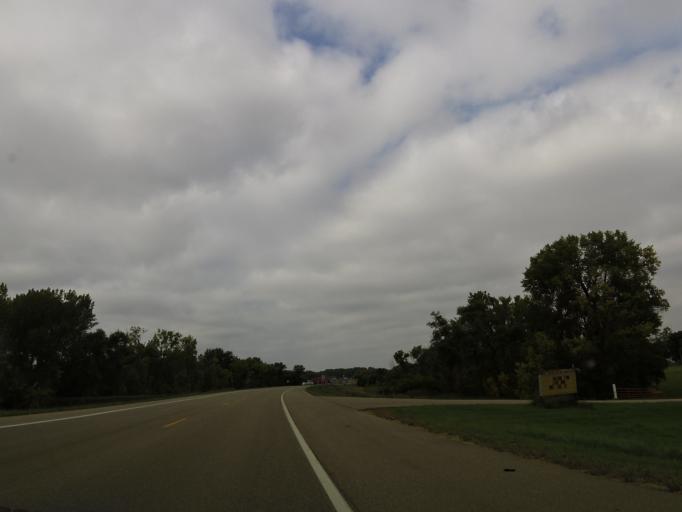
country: US
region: Minnesota
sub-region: Chippewa County
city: Montevideo
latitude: 44.9333
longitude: -95.7218
